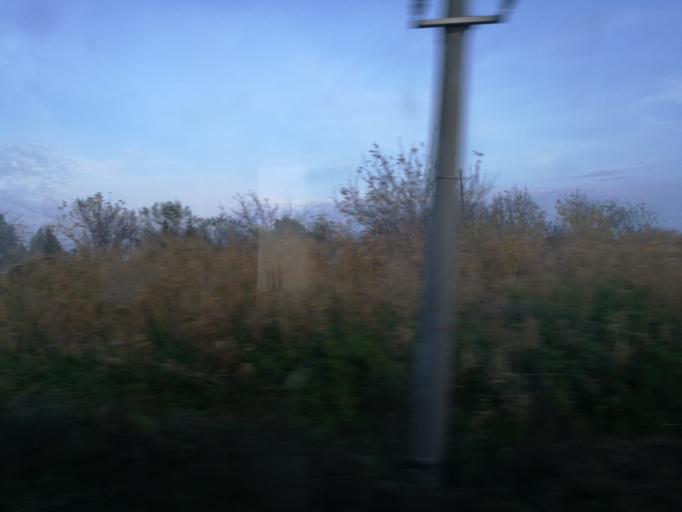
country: RO
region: Buzau
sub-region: Comuna Sahateni
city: Sahateni
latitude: 45.0317
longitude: 26.5239
